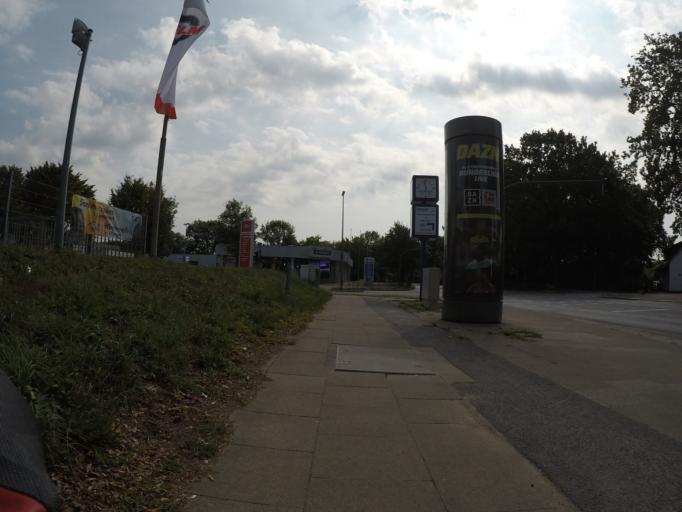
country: DE
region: Hamburg
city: Poppenbuettel
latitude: 53.6678
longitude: 10.0677
